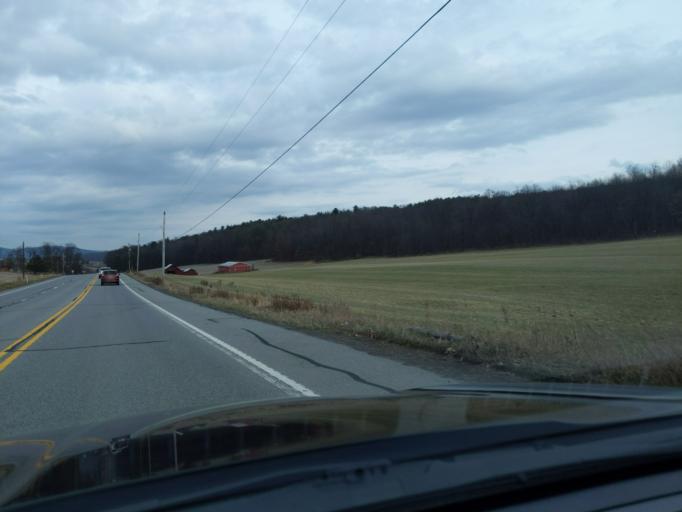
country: US
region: Pennsylvania
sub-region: Blair County
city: Williamsburg
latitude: 40.5093
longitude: -78.2184
